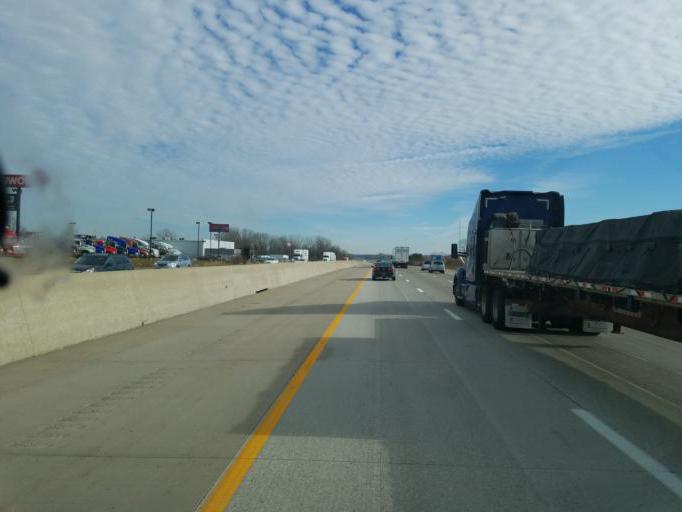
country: US
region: Ohio
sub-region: Clark County
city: Park Layne
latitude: 39.8659
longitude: -84.0708
